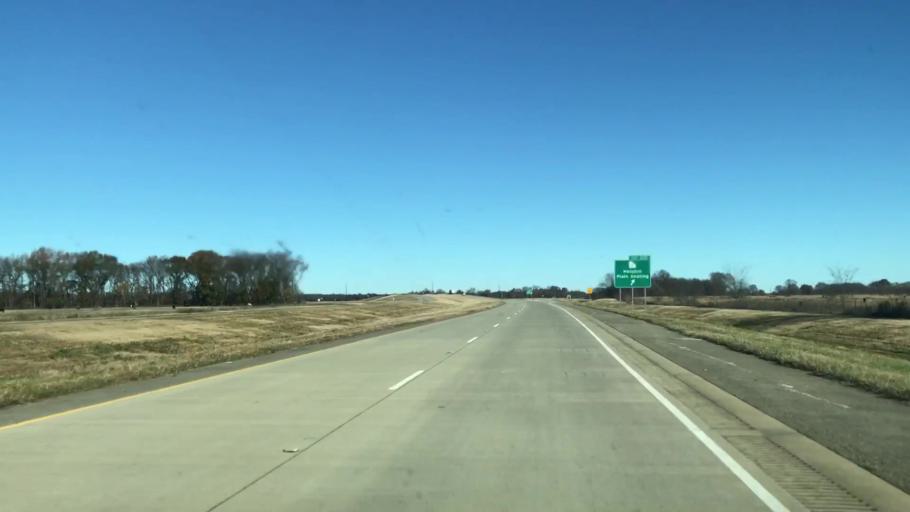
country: US
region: Louisiana
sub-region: Caddo Parish
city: Vivian
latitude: 32.8886
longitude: -93.8598
